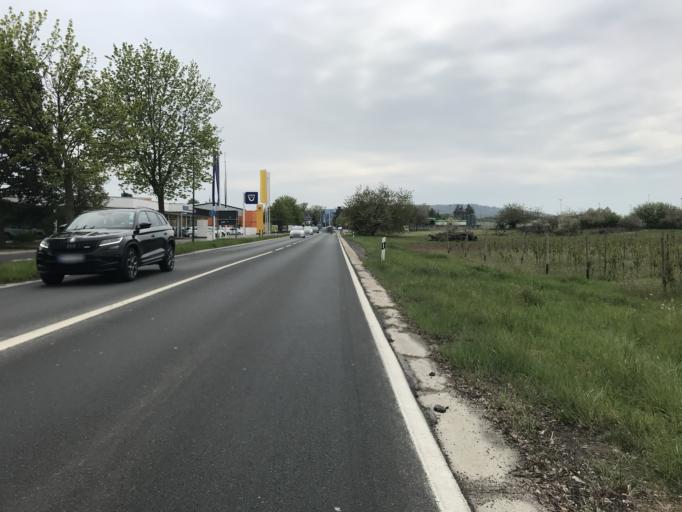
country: DE
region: Rheinland-Pfalz
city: Gau-Algesheim
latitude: 49.9669
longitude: 8.0186
